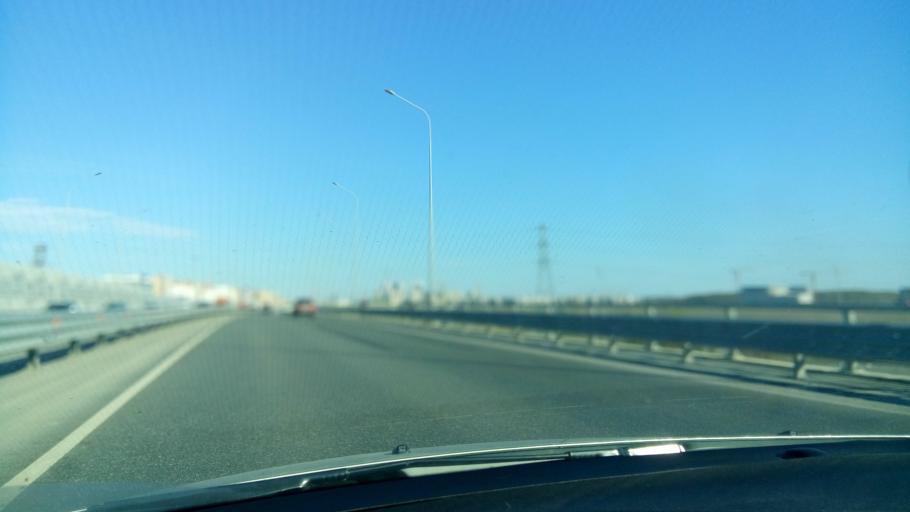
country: RU
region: Tjumen
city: Tyumen
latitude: 57.1136
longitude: 65.5380
